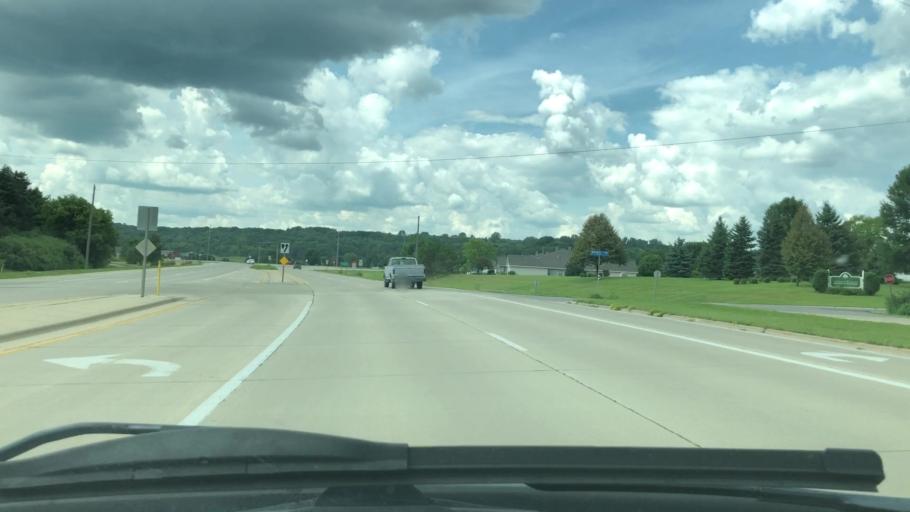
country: US
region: Minnesota
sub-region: Olmsted County
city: Rochester
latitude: 44.0025
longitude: -92.5036
